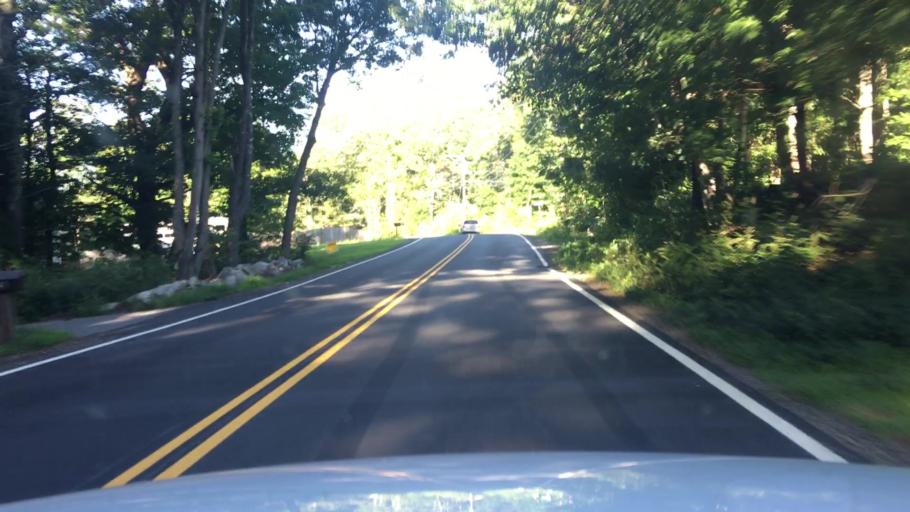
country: US
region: New Hampshire
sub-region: Rockingham County
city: Sandown
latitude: 42.9120
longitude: -71.1721
